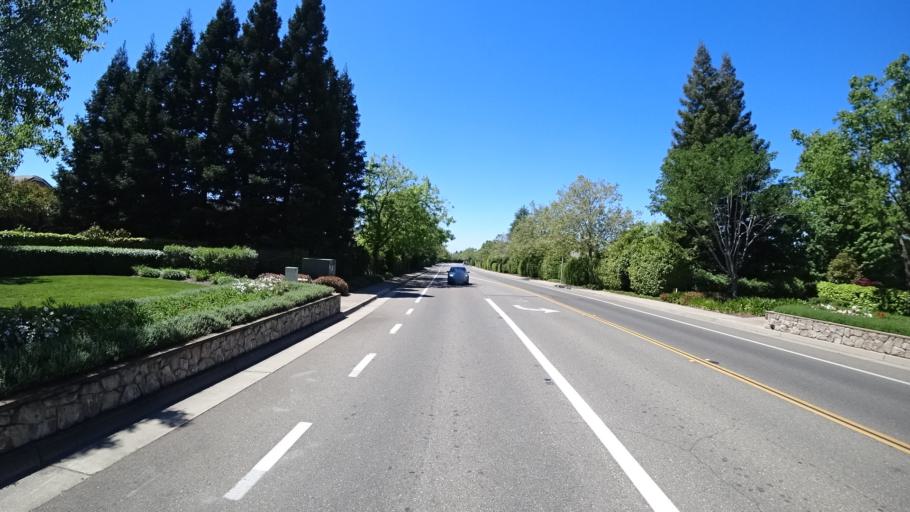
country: US
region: California
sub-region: Placer County
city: Rocklin
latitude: 38.8092
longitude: -121.2464
